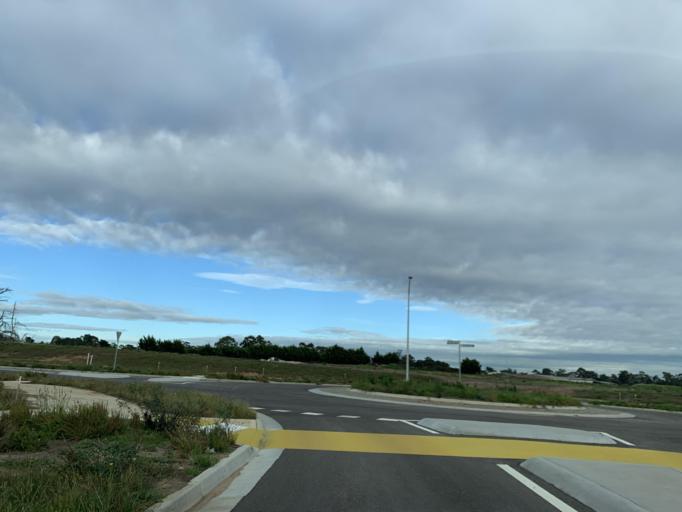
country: AU
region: Victoria
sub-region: Casey
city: Junction Village
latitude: -38.1298
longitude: 145.3365
